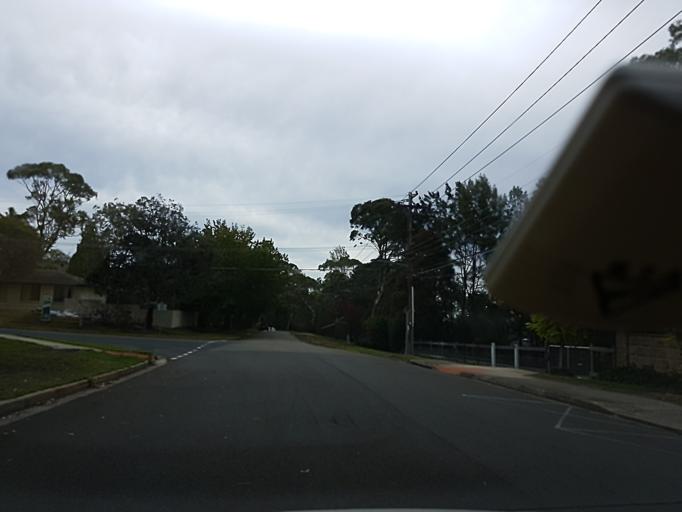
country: AU
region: New South Wales
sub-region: Warringah
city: Davidson
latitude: -33.7234
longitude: 151.2141
